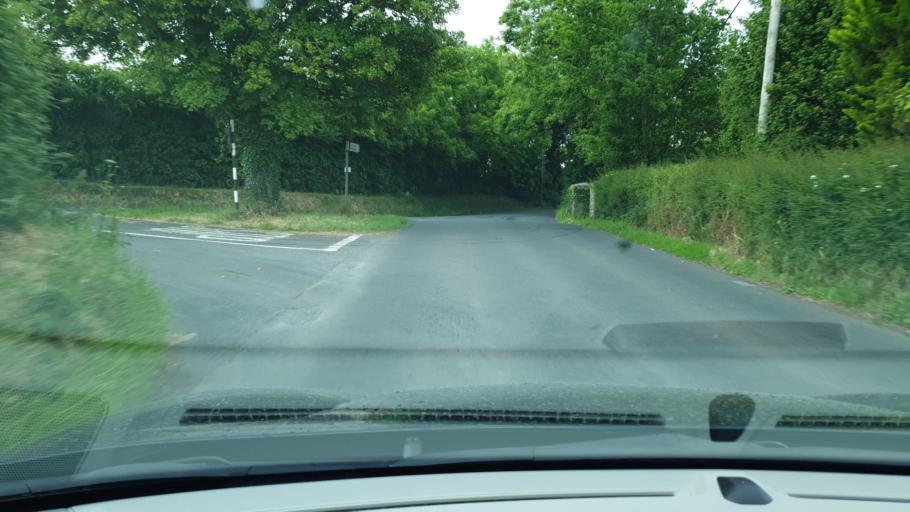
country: IE
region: Leinster
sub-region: An Mhi
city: Ashbourne
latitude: 53.5344
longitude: -6.4061
